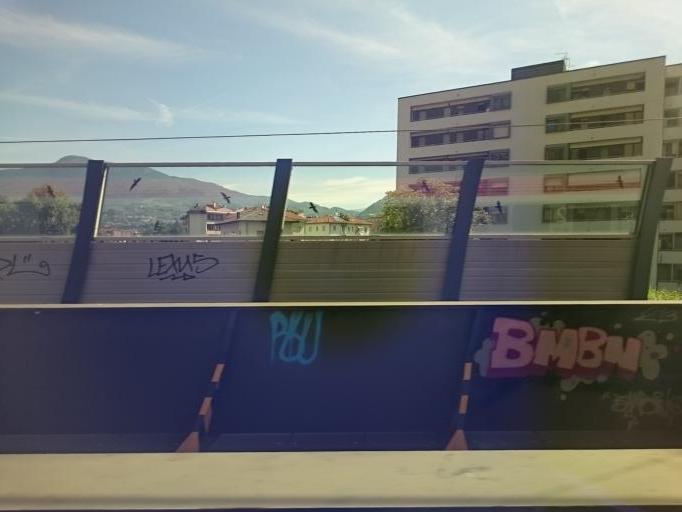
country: IT
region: Trentino-Alto Adige
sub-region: Provincia di Trento
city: Ravina
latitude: 46.0504
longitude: 11.1201
